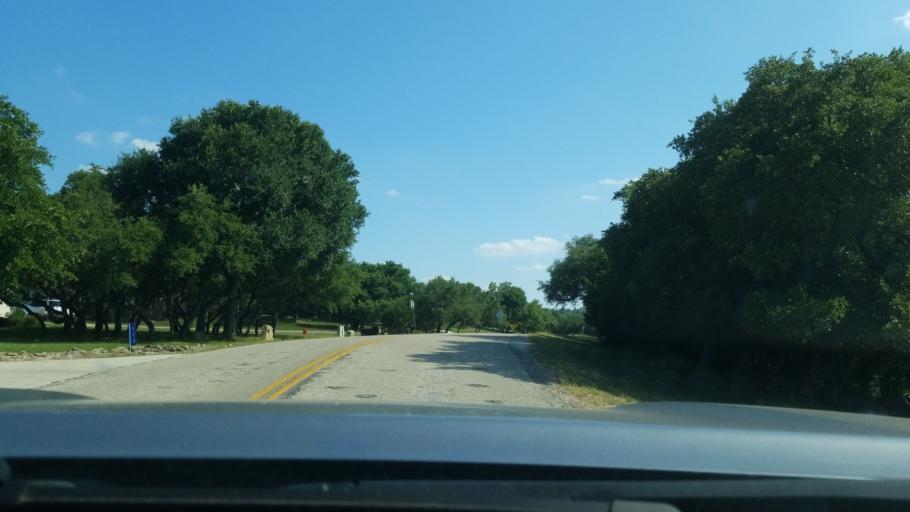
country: US
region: Texas
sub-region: Comal County
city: Bulverde
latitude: 29.8222
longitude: -98.3996
